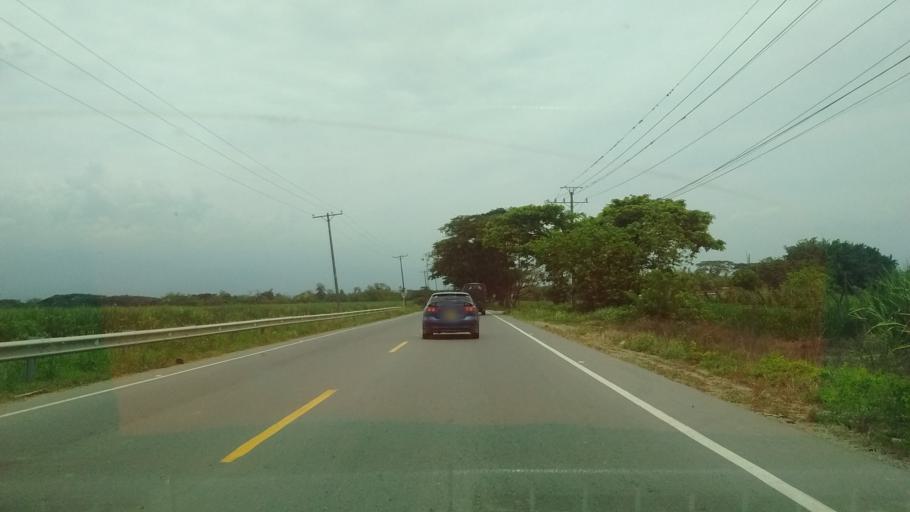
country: CO
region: Valle del Cauca
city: Jamundi
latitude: 3.2955
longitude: -76.4712
